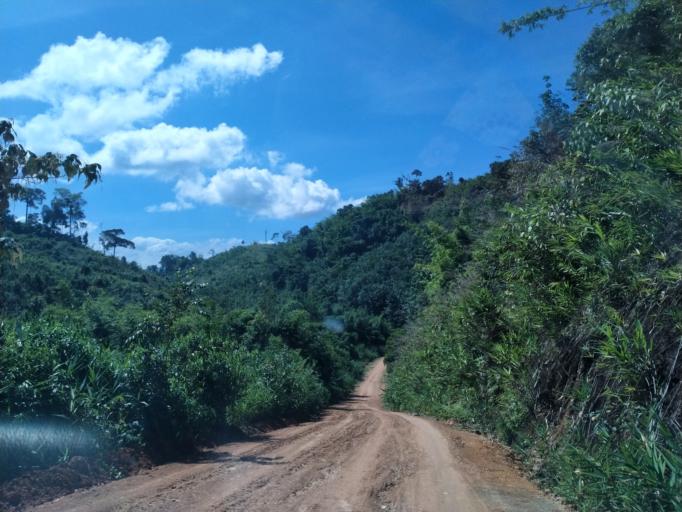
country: LA
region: Vientiane
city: Muang Phon-Hong
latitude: 18.6294
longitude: 102.8792
